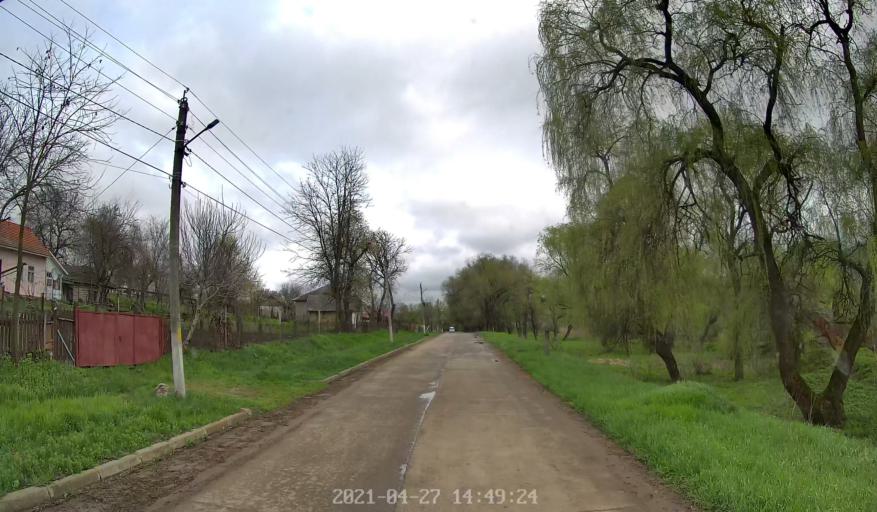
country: MD
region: Chisinau
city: Vadul lui Voda
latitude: 47.0496
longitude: 29.0499
